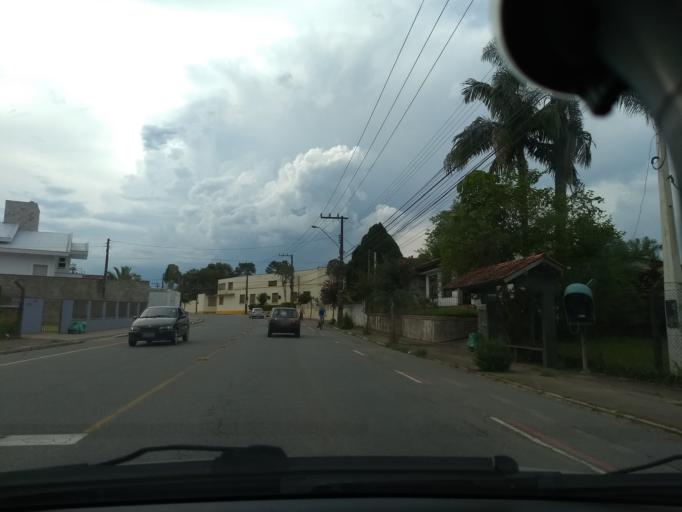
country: BR
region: Santa Catarina
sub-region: Jaragua Do Sul
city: Jaragua do Sul
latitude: -26.4733
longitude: -49.1024
